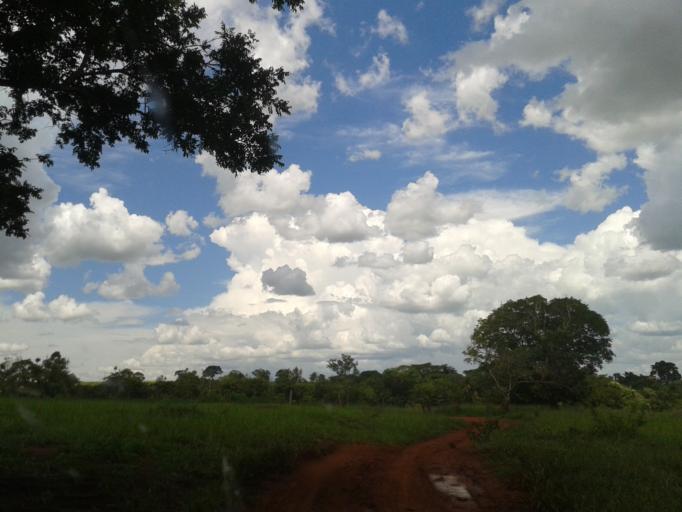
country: BR
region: Minas Gerais
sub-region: Capinopolis
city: Capinopolis
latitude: -18.7884
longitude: -49.8038
